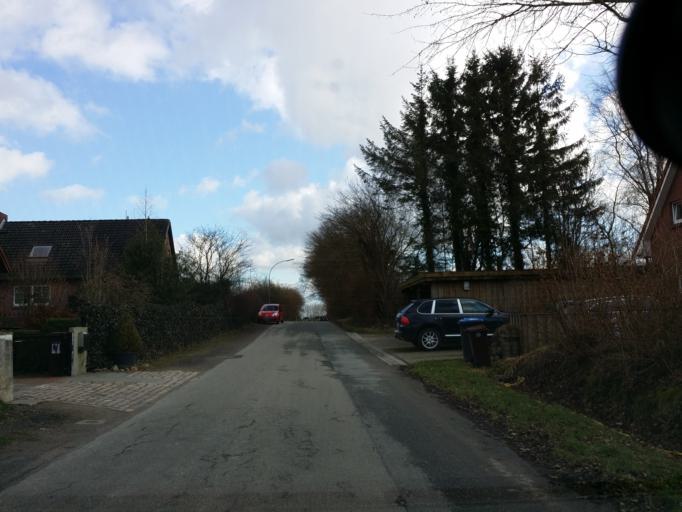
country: DE
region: Schleswig-Holstein
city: Krummwisch
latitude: 54.3104
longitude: 9.9031
